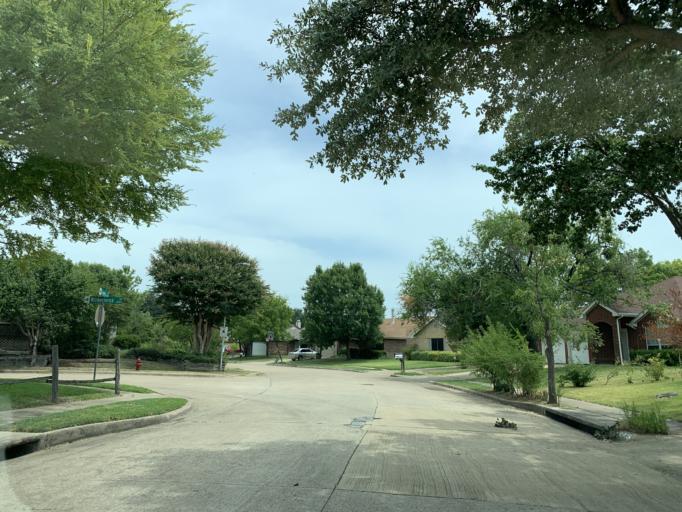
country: US
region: Texas
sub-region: Dallas County
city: Cedar Hill
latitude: 32.6530
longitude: -97.0251
